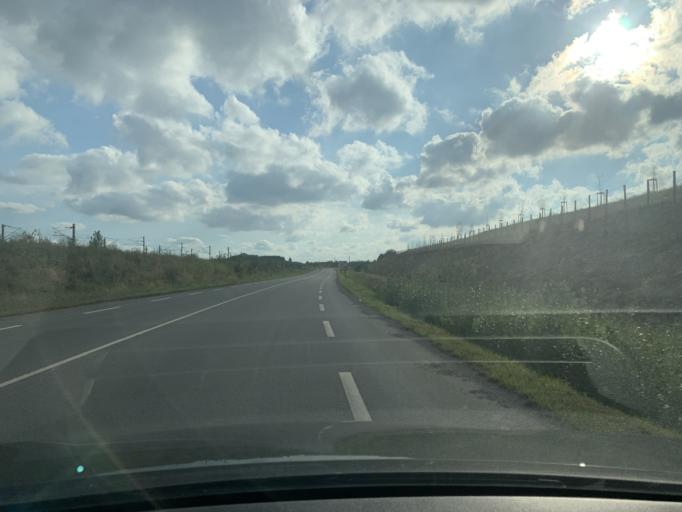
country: FR
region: Nord-Pas-de-Calais
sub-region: Departement du Pas-de-Calais
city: Evin-Malmaison
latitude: 50.4458
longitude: 3.0162
